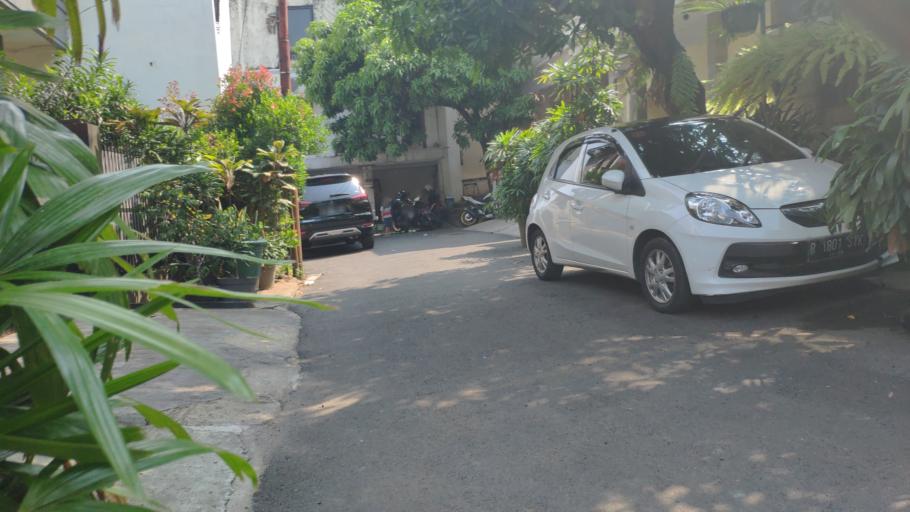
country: ID
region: Jakarta Raya
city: Jakarta
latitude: -6.2524
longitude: 106.7926
